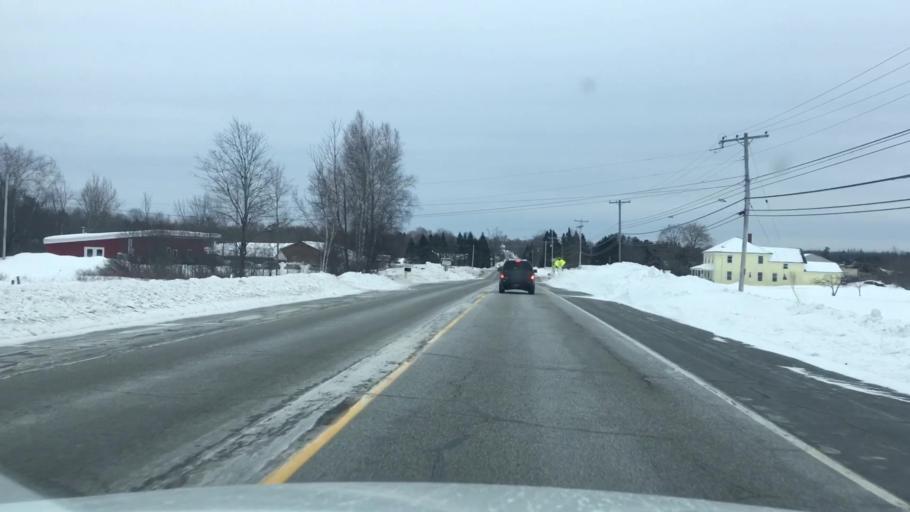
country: US
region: Maine
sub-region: Penobscot County
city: Charleston
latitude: 45.0194
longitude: -69.0286
